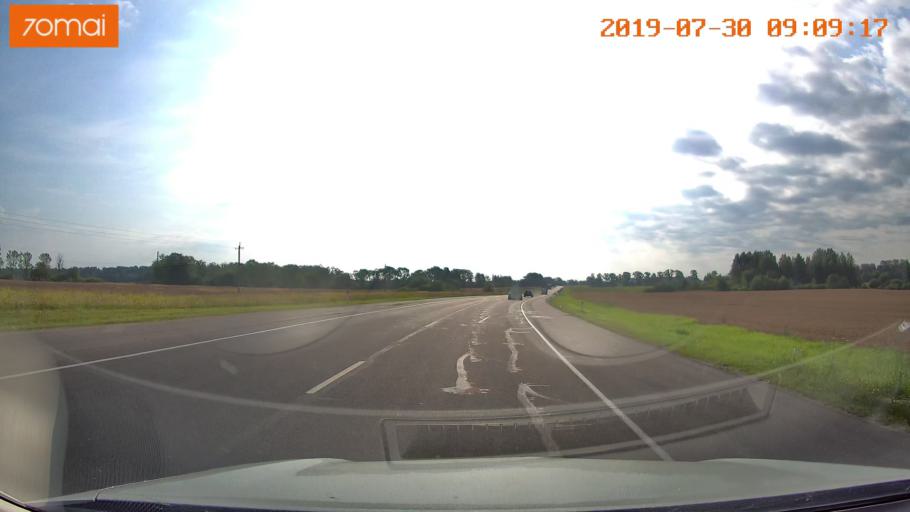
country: RU
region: Kaliningrad
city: Nesterov
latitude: 54.6138
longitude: 22.4063
